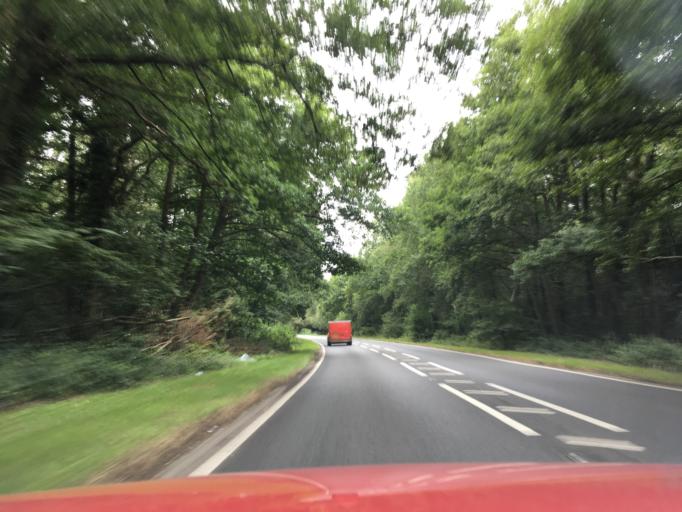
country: GB
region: England
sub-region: West Sussex
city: Crawley Down
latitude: 51.1444
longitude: -0.0688
